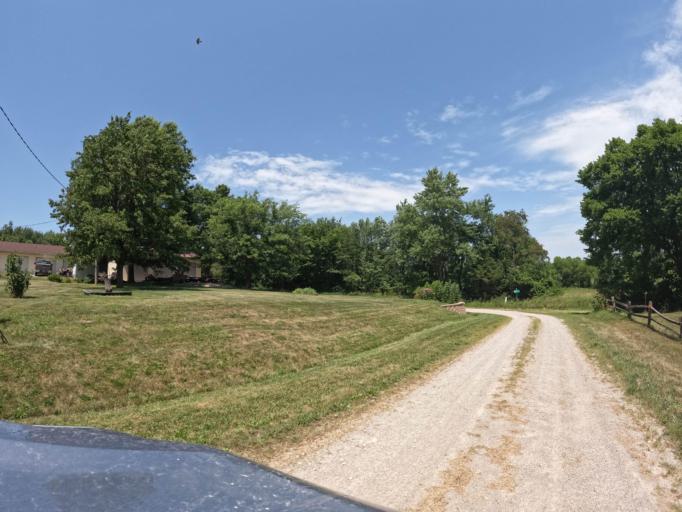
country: US
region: Iowa
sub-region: Appanoose County
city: Centerville
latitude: 40.7860
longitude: -92.9039
